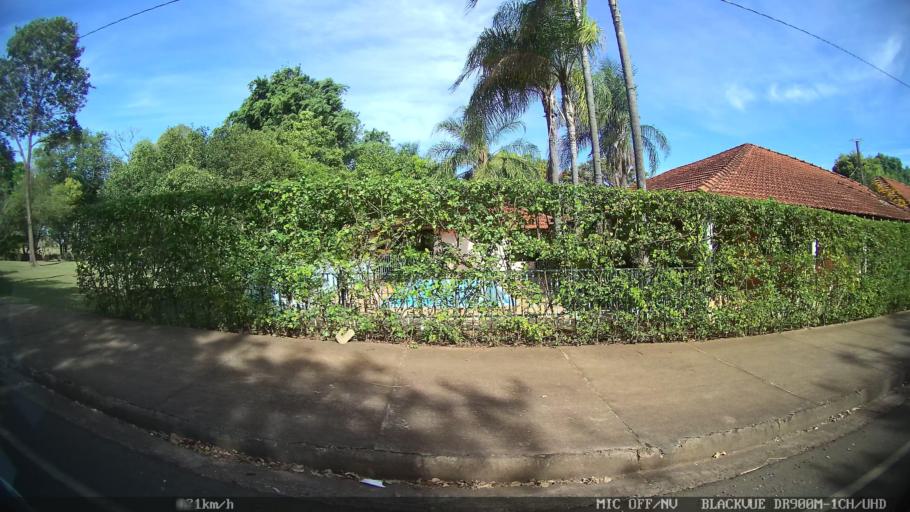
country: BR
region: Sao Paulo
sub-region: Sao Jose Do Rio Preto
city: Sao Jose do Rio Preto
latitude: -20.7962
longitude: -49.3175
